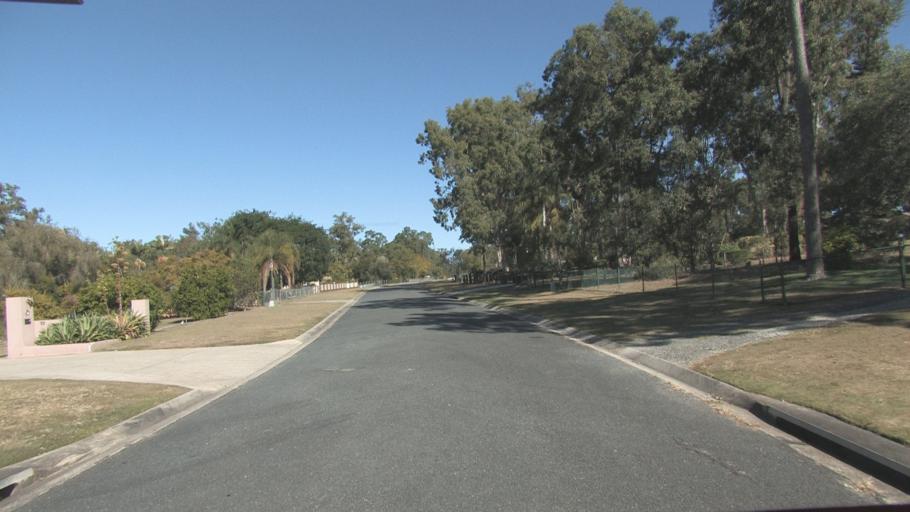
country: AU
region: Queensland
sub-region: Logan
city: North Maclean
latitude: -27.8193
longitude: 152.9481
